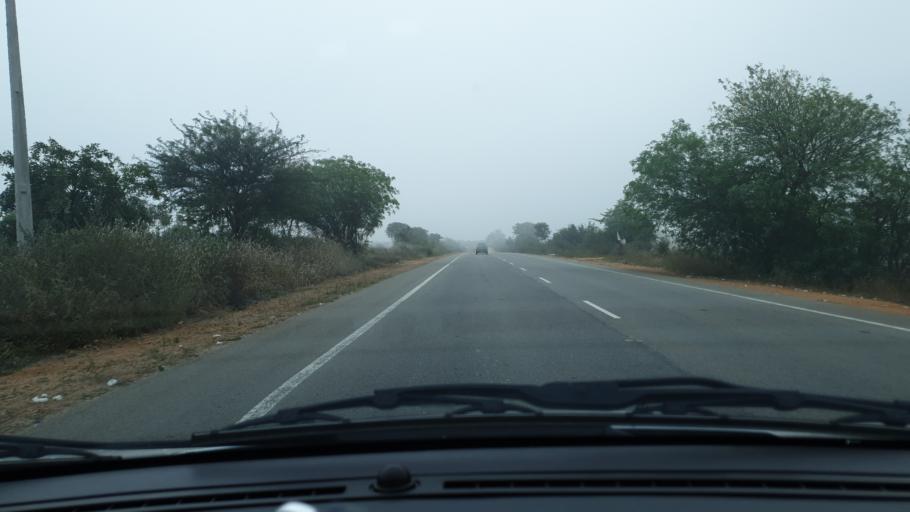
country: IN
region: Telangana
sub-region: Nalgonda
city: Devarkonda
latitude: 16.6327
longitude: 78.6411
